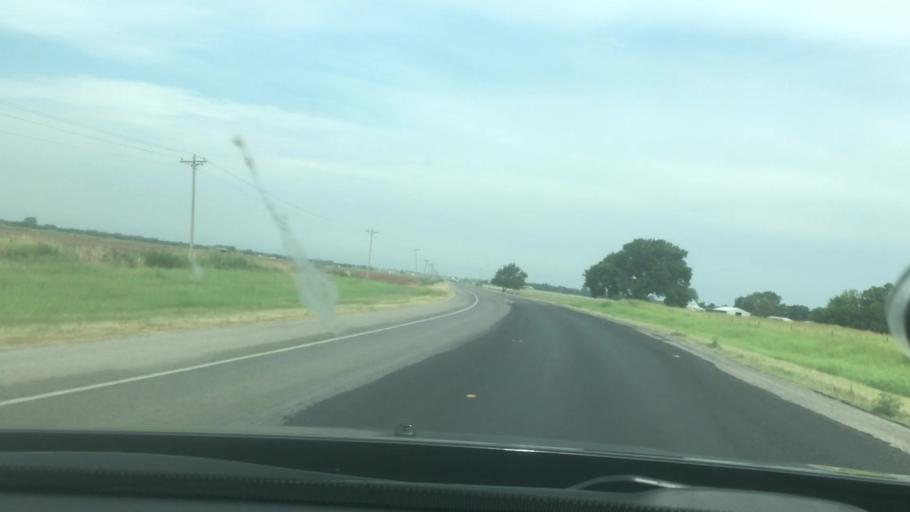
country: US
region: Oklahoma
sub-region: Garvin County
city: Maysville
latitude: 34.8214
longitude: -97.4956
